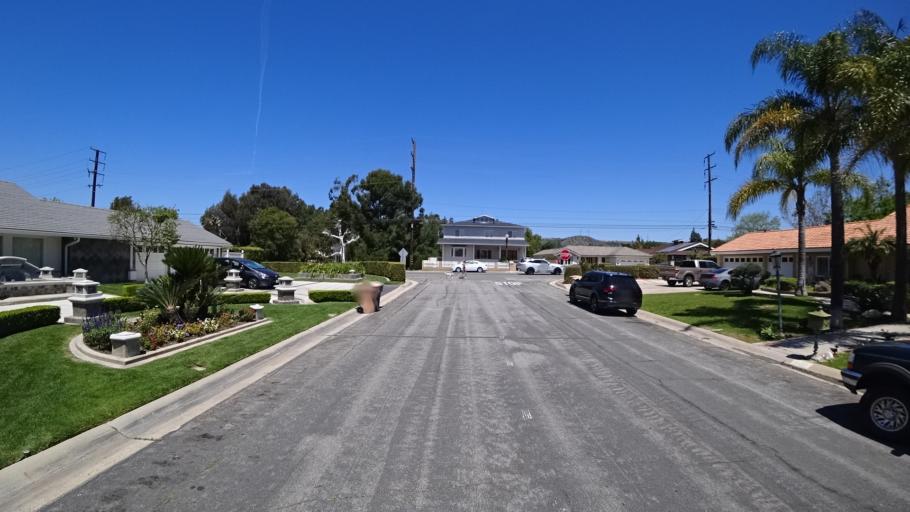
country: US
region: California
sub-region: Orange County
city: Villa Park
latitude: 33.8140
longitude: -117.8107
